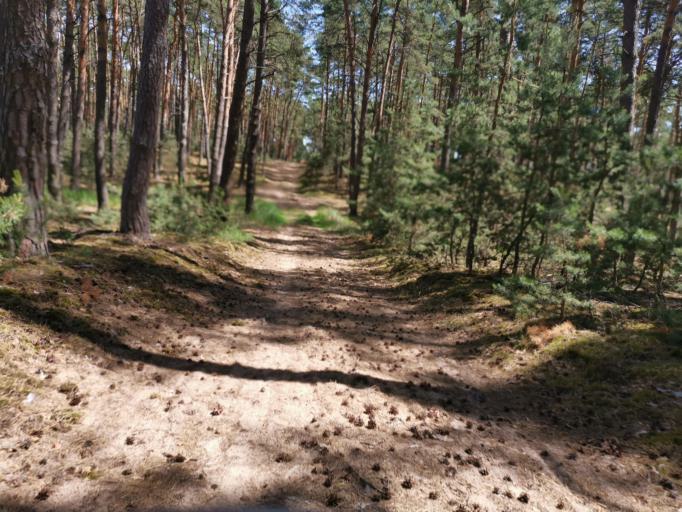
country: CZ
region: South Moravian
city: Bzenec
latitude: 48.9373
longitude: 17.2568
